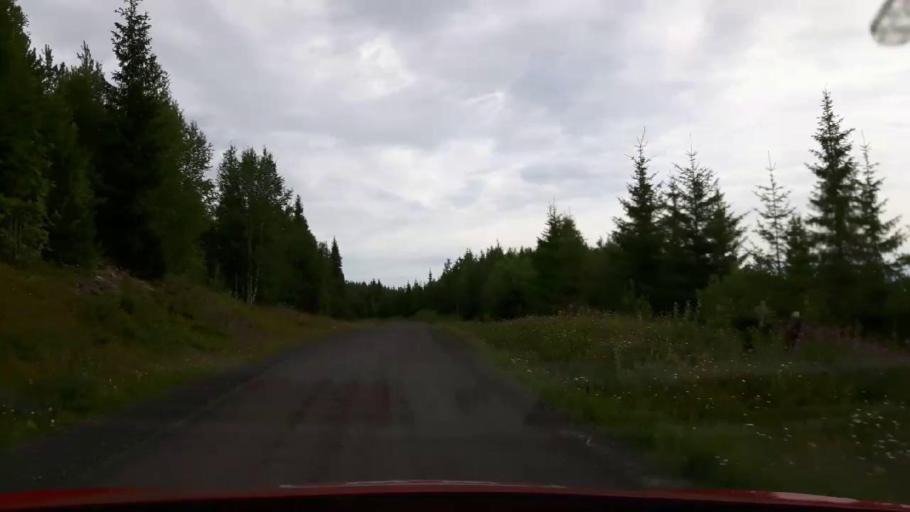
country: SE
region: Jaemtland
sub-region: OEstersunds Kommun
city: Lit
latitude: 63.3992
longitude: 15.2291
